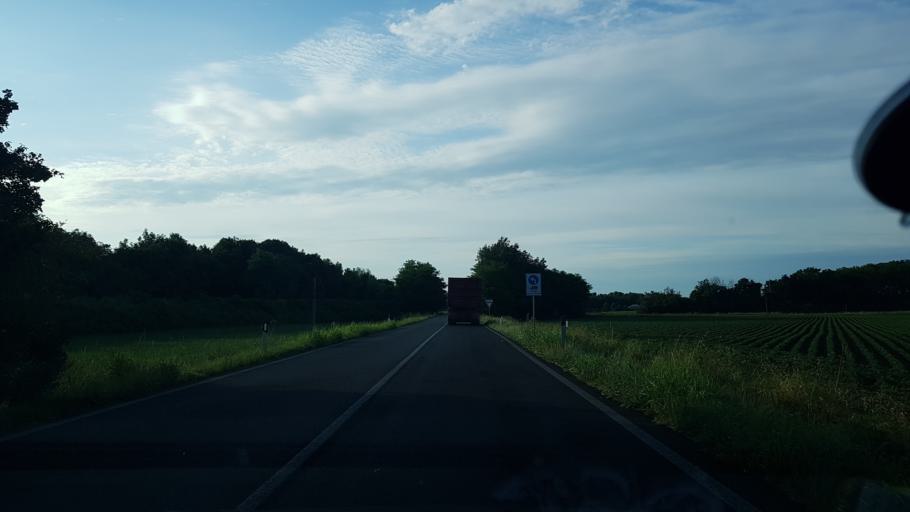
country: IT
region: Friuli Venezia Giulia
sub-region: Provincia di Udine
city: Chiopris
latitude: 45.9181
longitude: 13.4088
